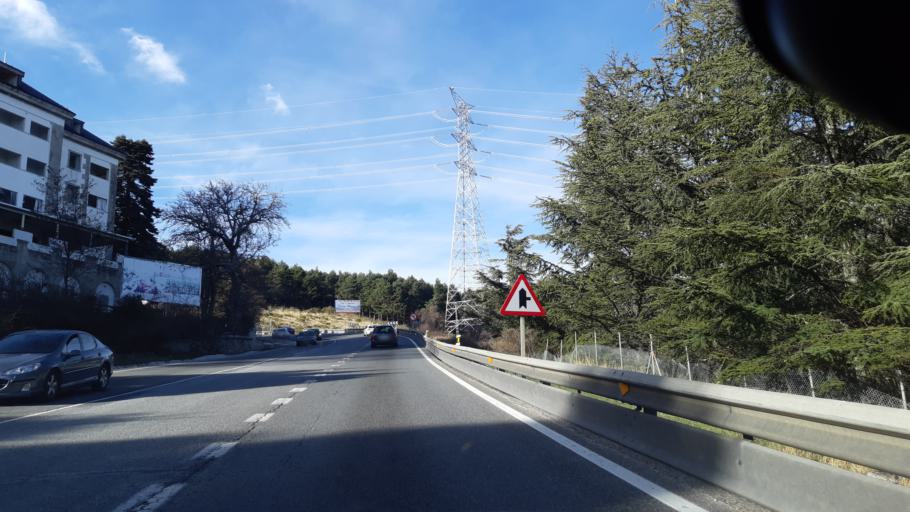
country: ES
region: Madrid
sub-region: Provincia de Madrid
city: Guadarrama
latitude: 40.7081
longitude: -4.1275
